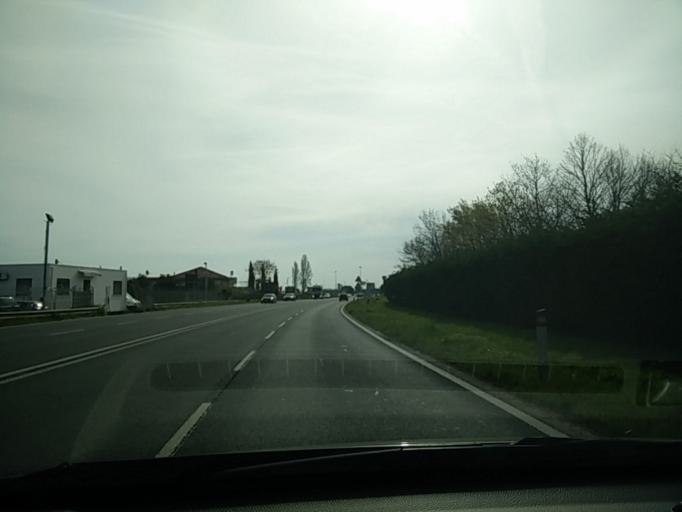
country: IT
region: Emilia-Romagna
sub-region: Provincia di Rimini
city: Santa Giustina
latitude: 44.0701
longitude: 12.5161
